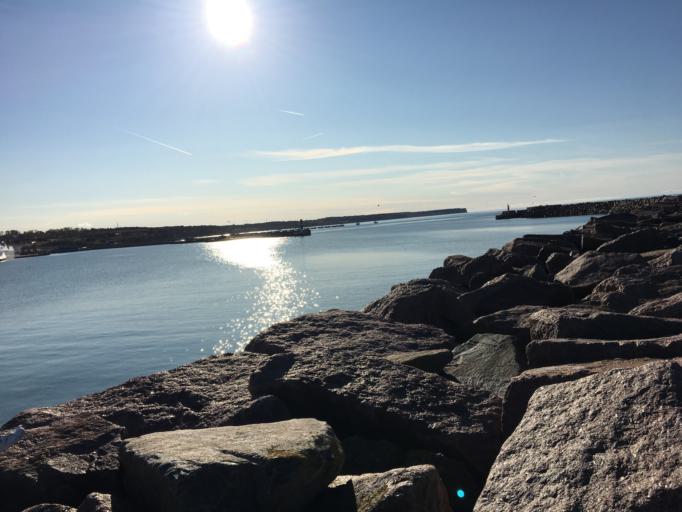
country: SE
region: Gotland
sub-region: Gotland
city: Visby
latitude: 57.6377
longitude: 18.2769
